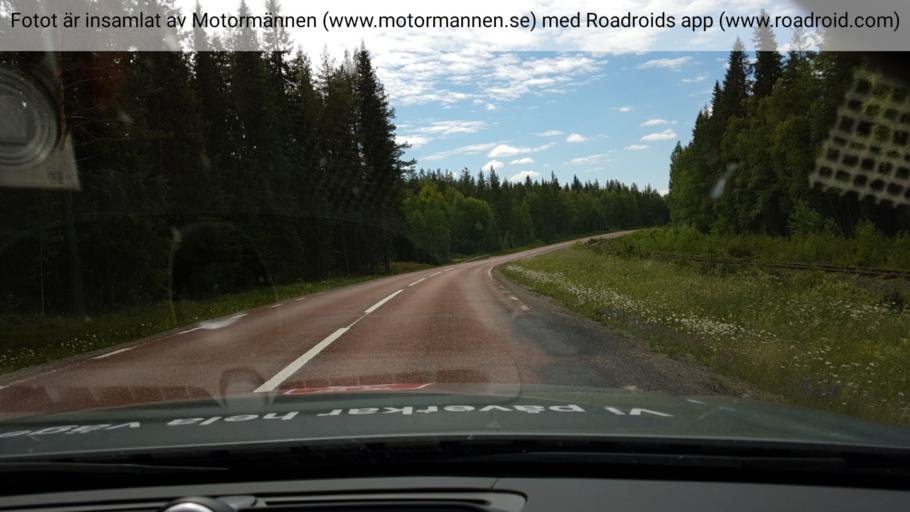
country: SE
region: Jaemtland
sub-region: Stroemsunds Kommun
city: Stroemsund
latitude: 64.0305
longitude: 15.9676
